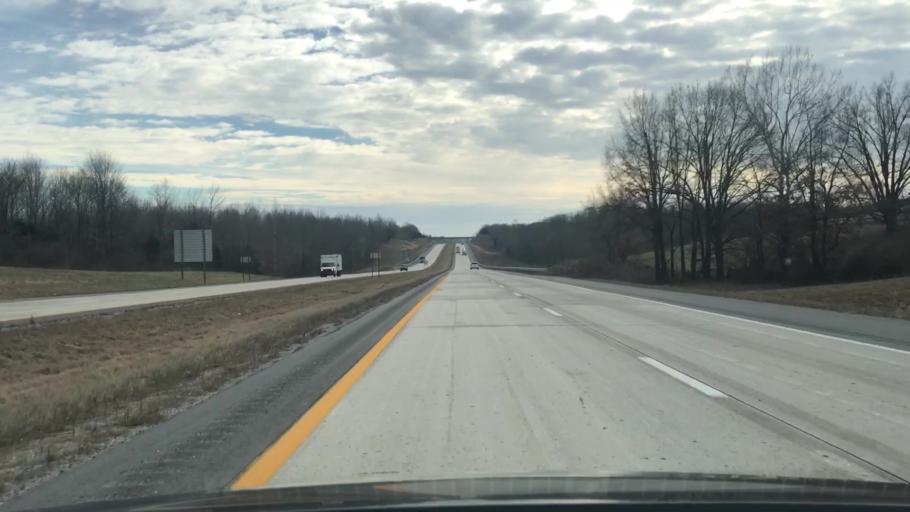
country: US
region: Kentucky
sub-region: Ohio County
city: Beaver Dam
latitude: 37.4417
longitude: -86.8595
